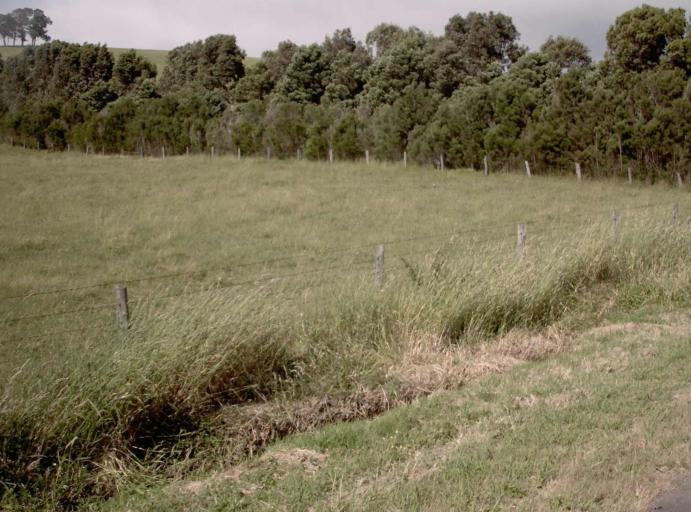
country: AU
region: Victoria
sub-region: Latrobe
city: Traralgon
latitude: -38.1497
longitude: 146.4603
